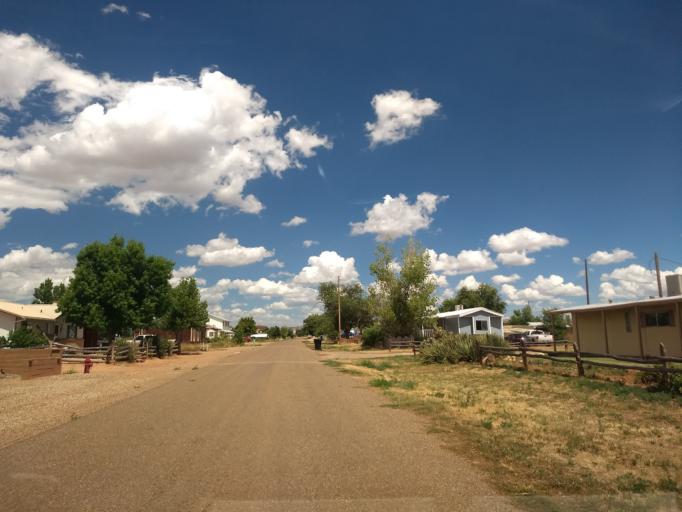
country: US
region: Arizona
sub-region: Coconino County
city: Fredonia
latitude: 36.9410
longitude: -112.5205
